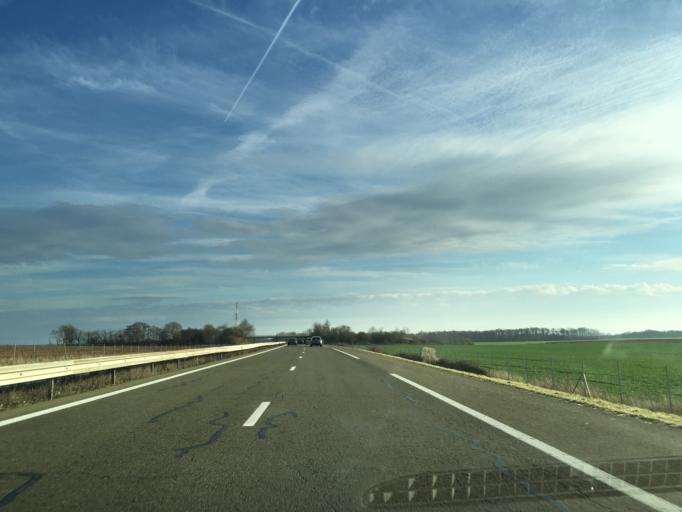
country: FR
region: Picardie
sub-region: Departement de l'Aisne
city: Montreuil-aux-Lions
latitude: 49.0395
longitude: 3.2261
